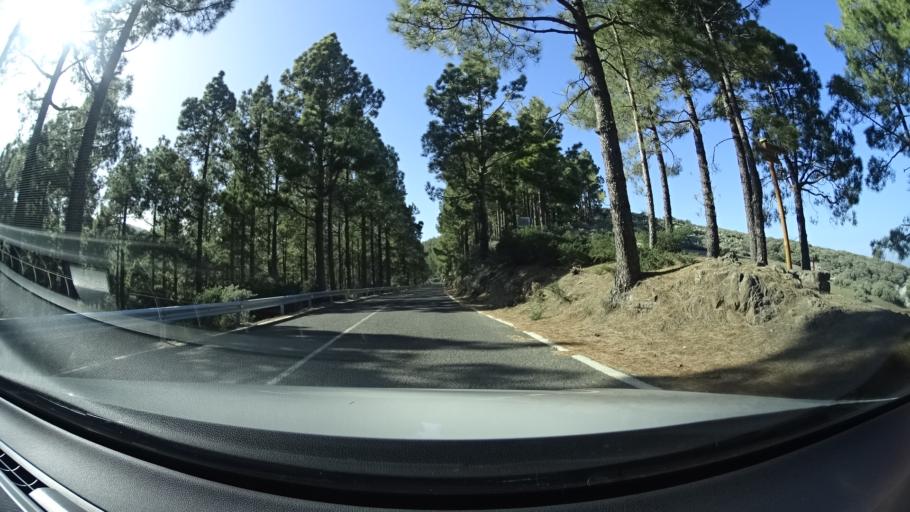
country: ES
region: Canary Islands
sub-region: Provincia de Las Palmas
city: Vega de San Mateo
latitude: 27.9650
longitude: -15.5421
